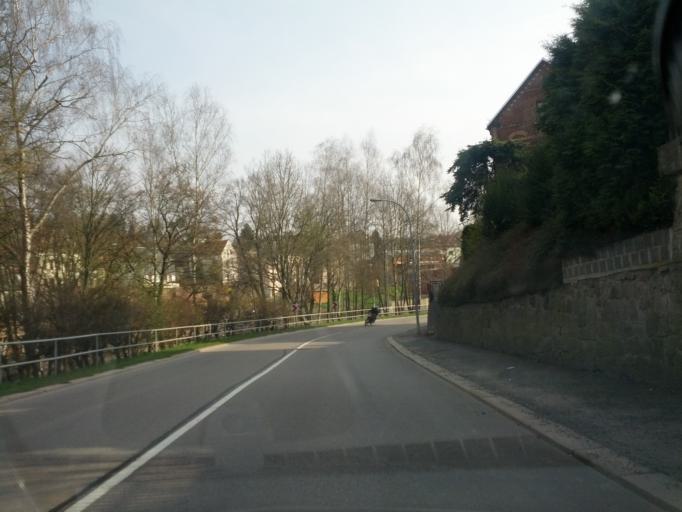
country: DE
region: Saxony
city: Kirchberg
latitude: 50.6210
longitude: 12.5333
